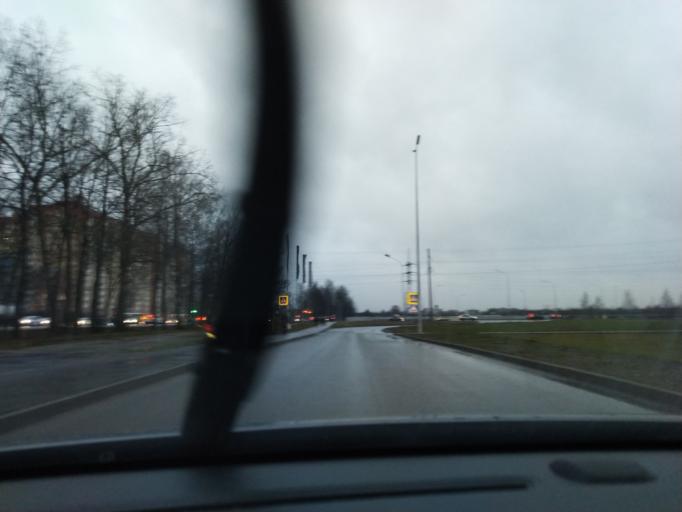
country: RU
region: St.-Petersburg
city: Gorelovo
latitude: 59.7925
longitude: 30.1471
